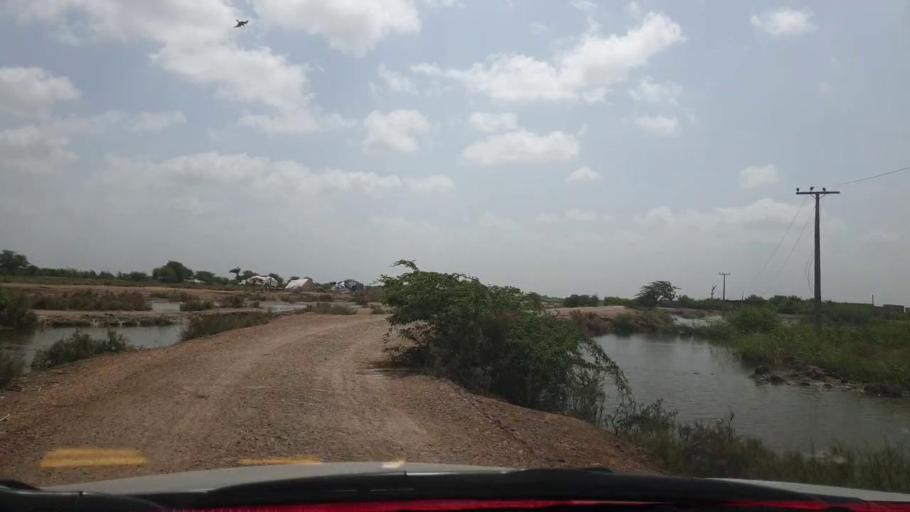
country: PK
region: Sindh
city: Talhar
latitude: 24.9033
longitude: 68.8593
